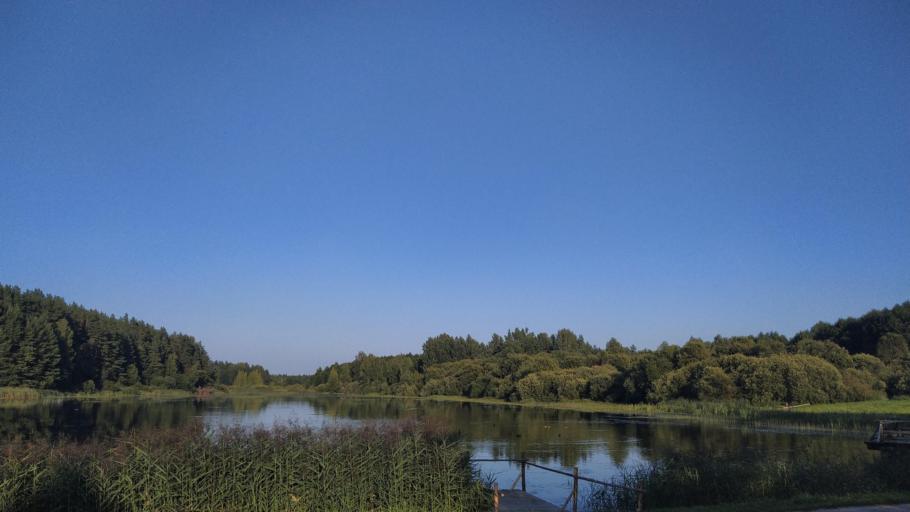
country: RU
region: Pskov
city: Pushkinskiye Gory
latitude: 57.0469
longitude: 28.9175
